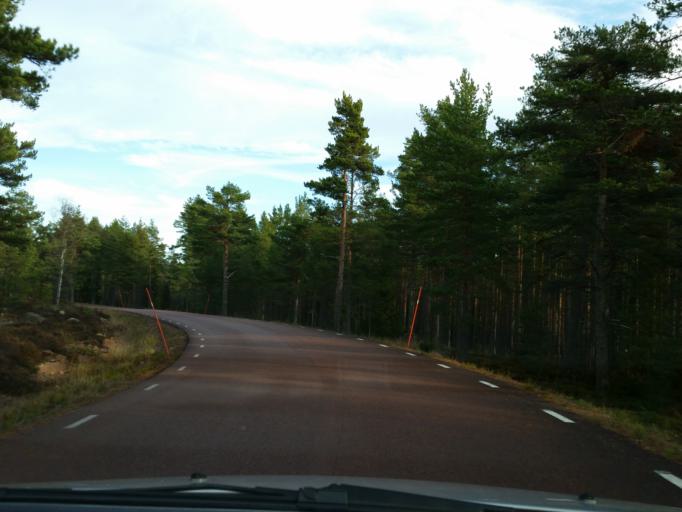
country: AX
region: Alands landsbygd
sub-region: Saltvik
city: Saltvik
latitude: 60.3325
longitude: 20.0860
